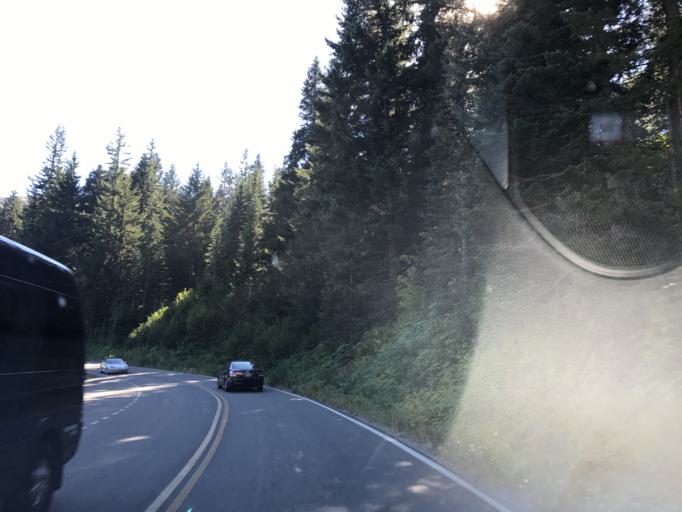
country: US
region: Washington
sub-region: Pierce County
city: Buckley
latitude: 46.7758
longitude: -121.7029
